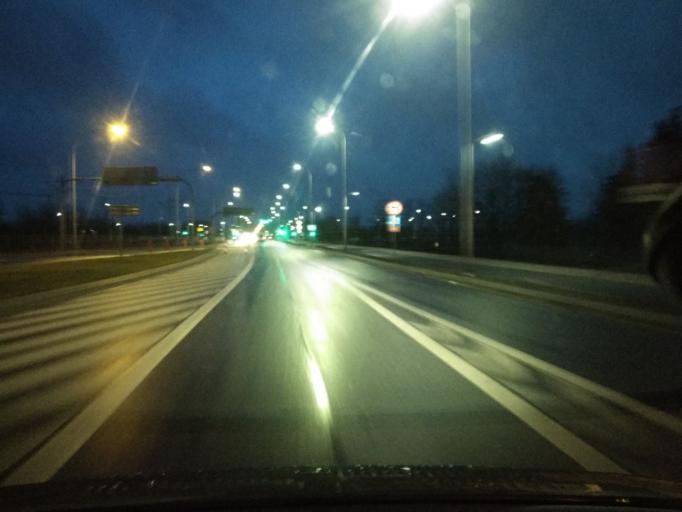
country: PL
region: Lower Silesian Voivodeship
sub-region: Powiat wroclawski
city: Smolec
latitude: 51.1387
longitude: 16.9319
